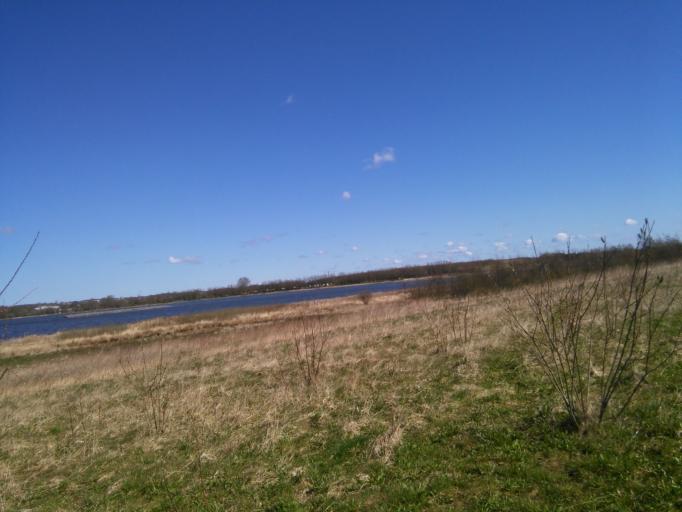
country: DK
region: Central Jutland
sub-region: Arhus Kommune
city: Lystrup
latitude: 56.2121
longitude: 10.2239
